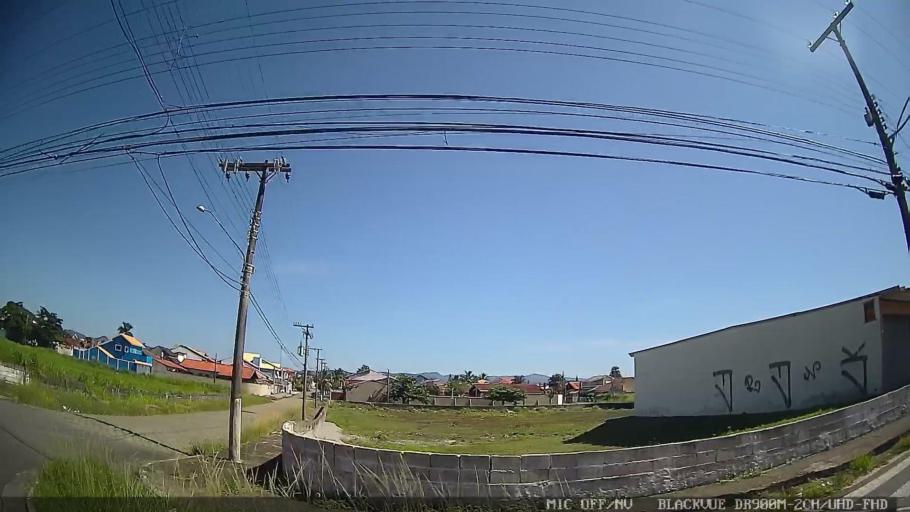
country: BR
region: Sao Paulo
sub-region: Peruibe
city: Peruibe
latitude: -24.2898
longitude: -46.9611
